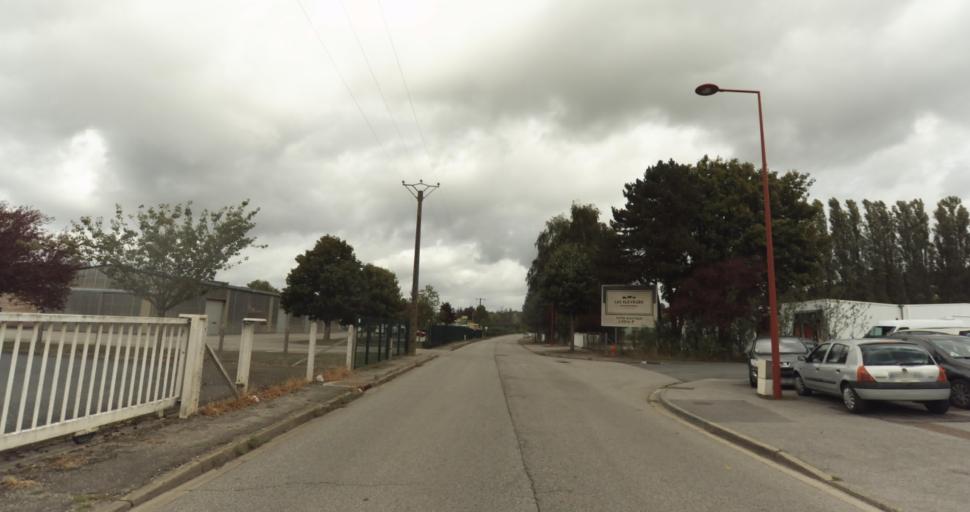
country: FR
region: Lower Normandy
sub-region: Departement de l'Orne
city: Gace
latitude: 48.7968
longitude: 0.2919
